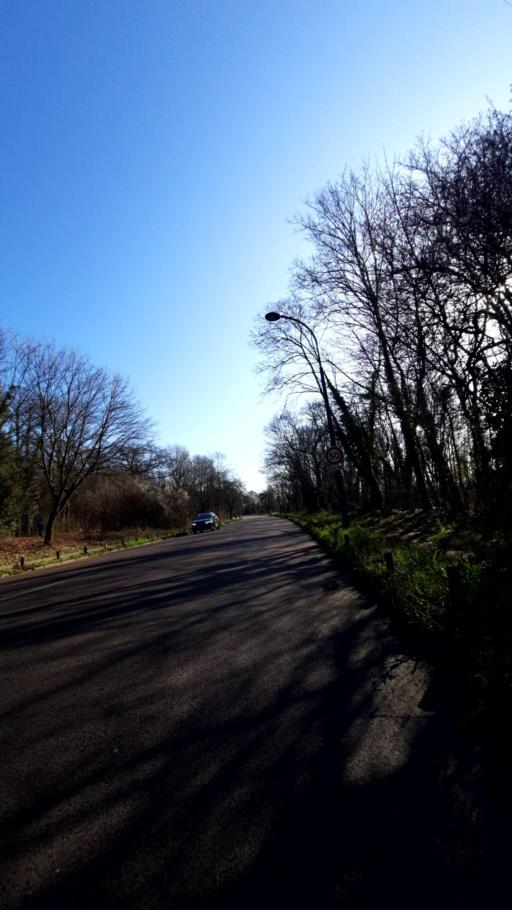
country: FR
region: Ile-de-France
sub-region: Departement du Val-de-Marne
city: Maisons-Alfort
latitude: 48.8193
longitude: 2.4375
